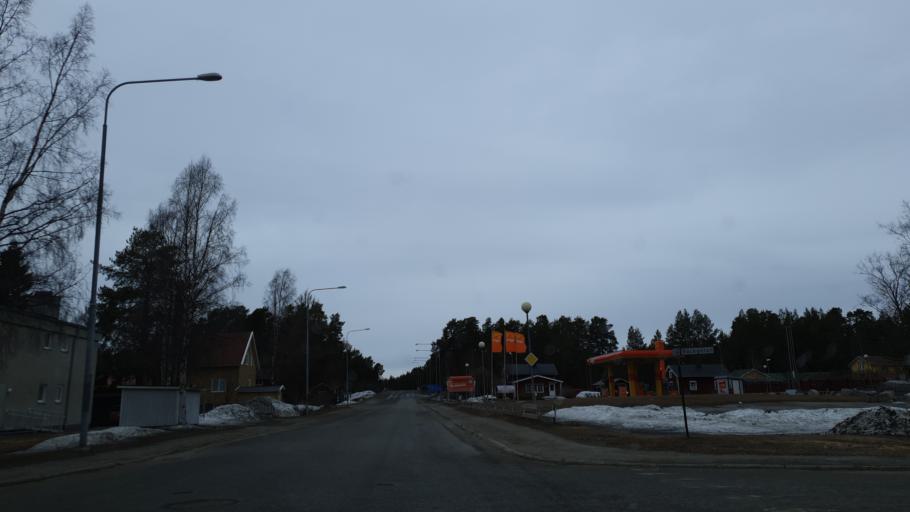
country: SE
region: Vaesterbotten
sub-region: Skelleftea Kommun
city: Byske
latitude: 64.9548
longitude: 21.2111
